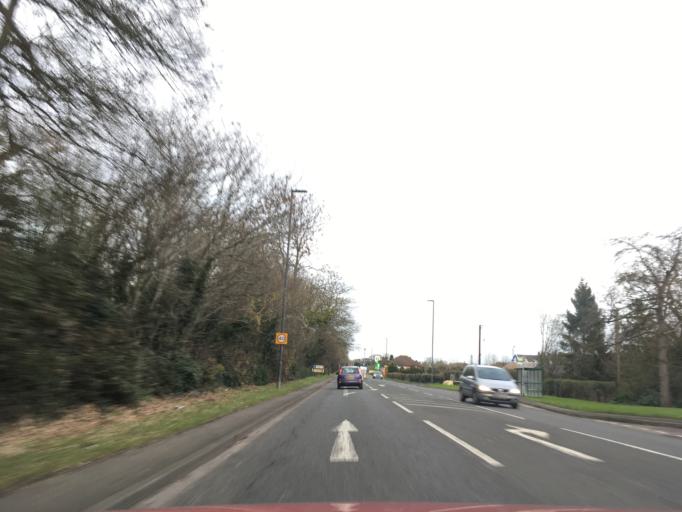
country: GB
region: England
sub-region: South Gloucestershire
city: Almondsbury
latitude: 51.5640
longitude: -2.5549
